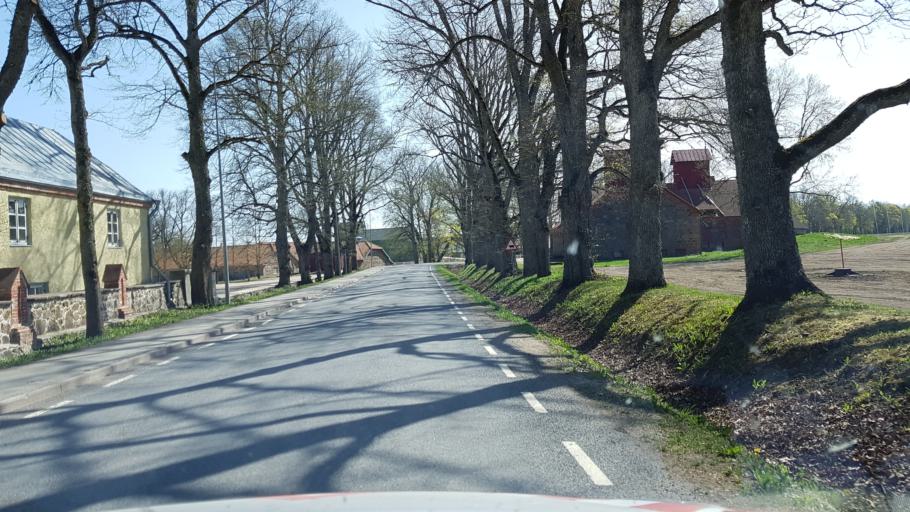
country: EE
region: Viljandimaa
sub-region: Vohma linn
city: Vohma
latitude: 58.5531
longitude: 25.5629
